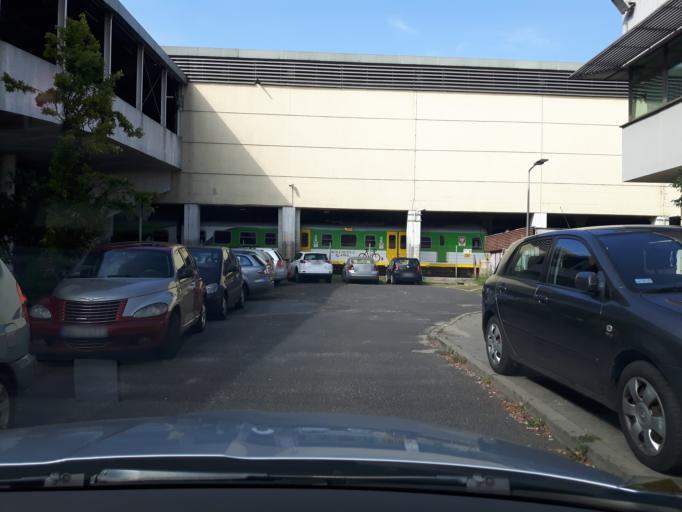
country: PL
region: Masovian Voivodeship
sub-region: Warszawa
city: Praga Polnoc
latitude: 52.2555
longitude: 21.0393
